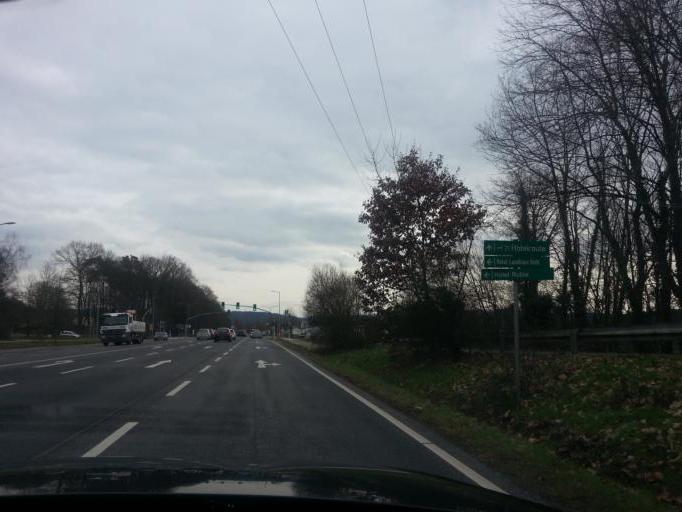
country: DE
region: Saarland
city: Homburg
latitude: 49.3354
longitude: 7.3118
